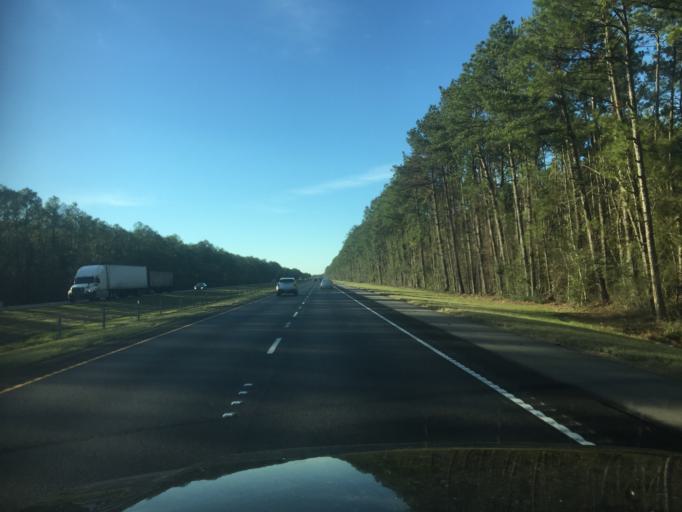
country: US
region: Louisiana
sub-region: Saint Tammany Parish
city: Lacombe
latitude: 30.3635
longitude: -89.9415
